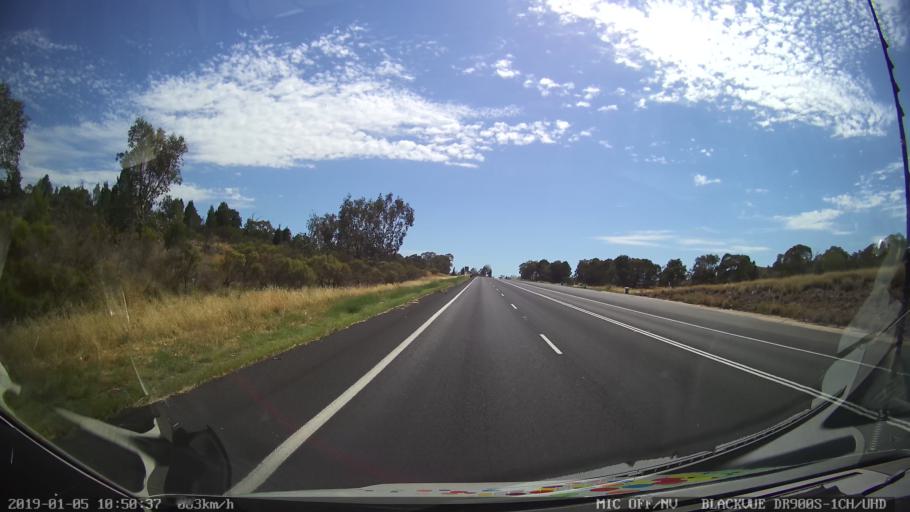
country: AU
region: New South Wales
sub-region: Warrumbungle Shire
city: Coonabarabran
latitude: -31.4279
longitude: 149.0777
